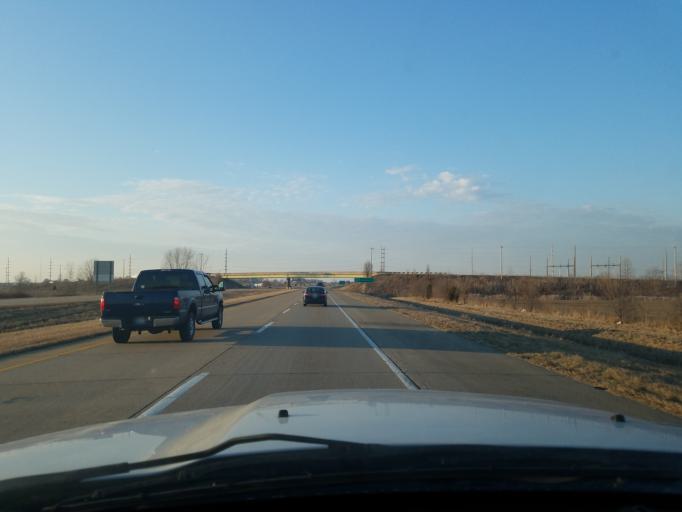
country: US
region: Indiana
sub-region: Vanderburgh County
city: Melody Hill
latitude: 37.9894
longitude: -87.4612
